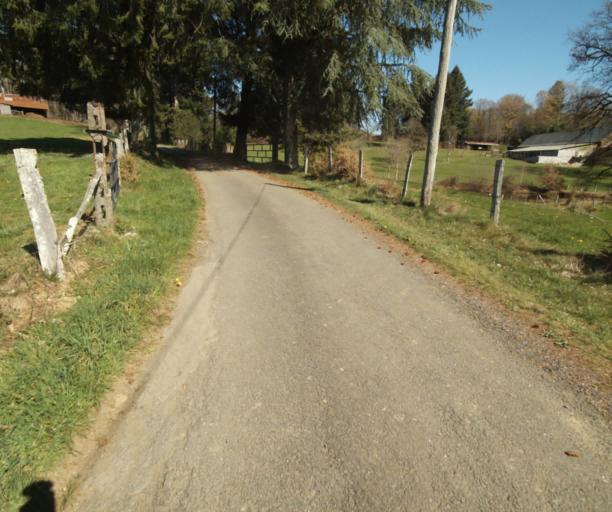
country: FR
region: Limousin
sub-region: Departement de la Correze
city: Saint-Clement
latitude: 45.3544
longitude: 1.6537
